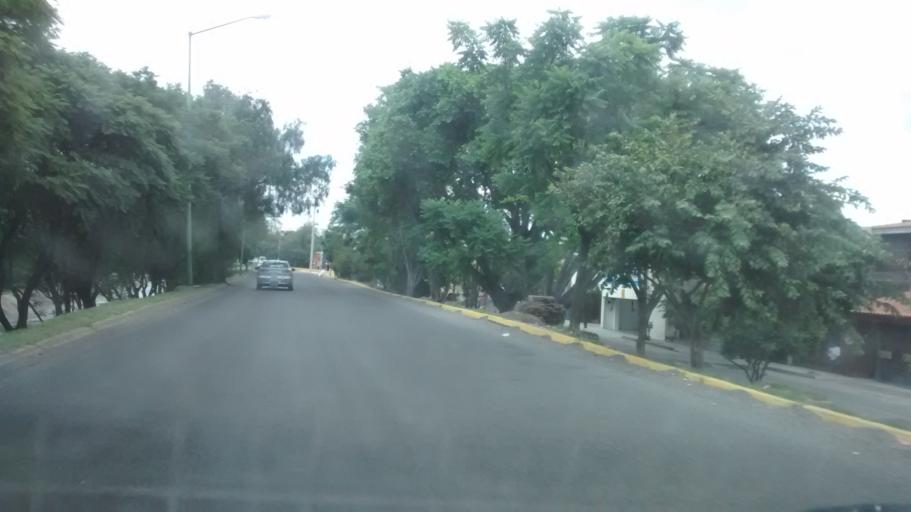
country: MX
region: Guanajuato
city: Leon
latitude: 21.1116
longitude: -101.6639
